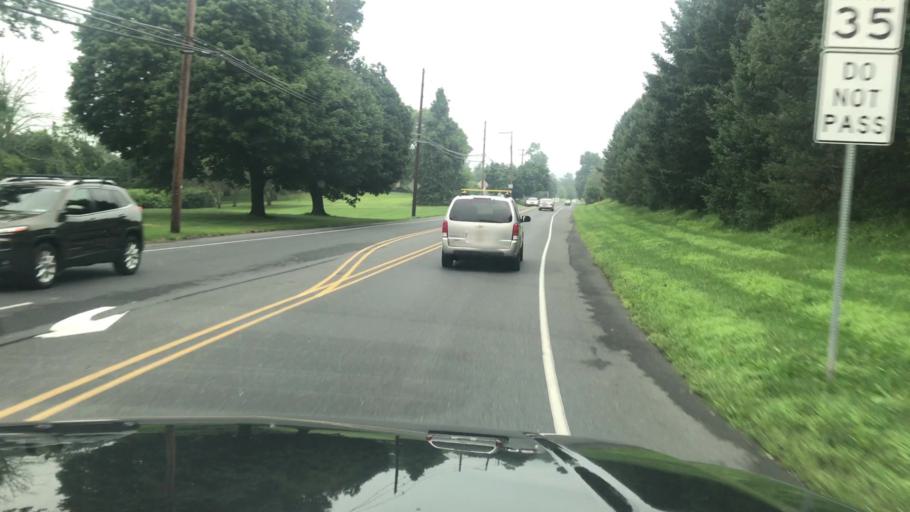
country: US
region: Pennsylvania
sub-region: Cumberland County
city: Enola
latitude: 40.2713
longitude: -76.9698
